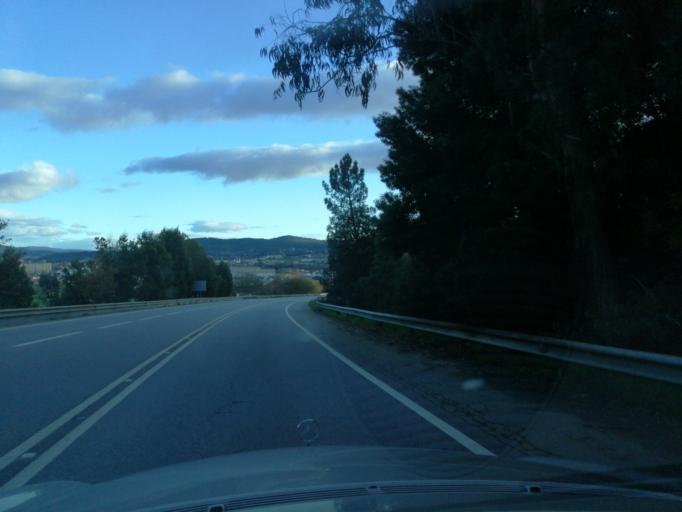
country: PT
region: Braga
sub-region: Barcelos
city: Vila Frescainha
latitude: 41.5392
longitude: -8.6404
